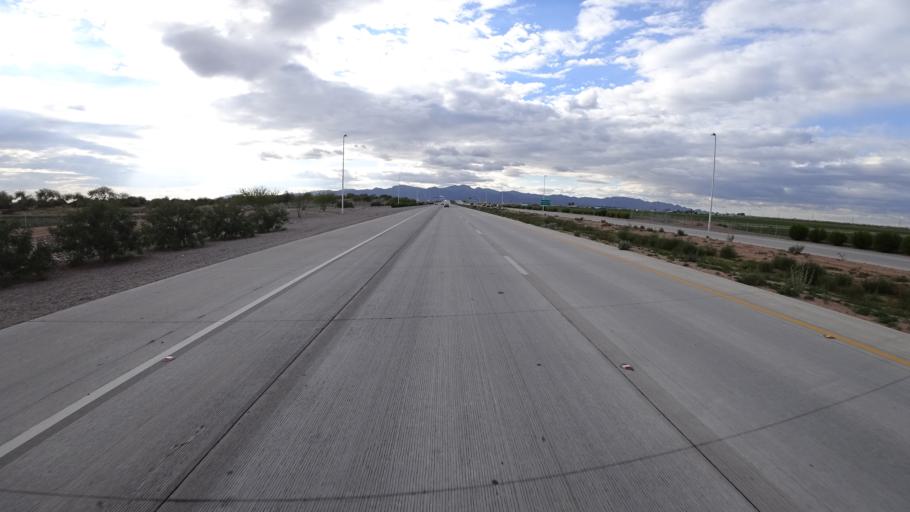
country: US
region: Arizona
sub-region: Maricopa County
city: Citrus Park
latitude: 33.5590
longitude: -112.3839
